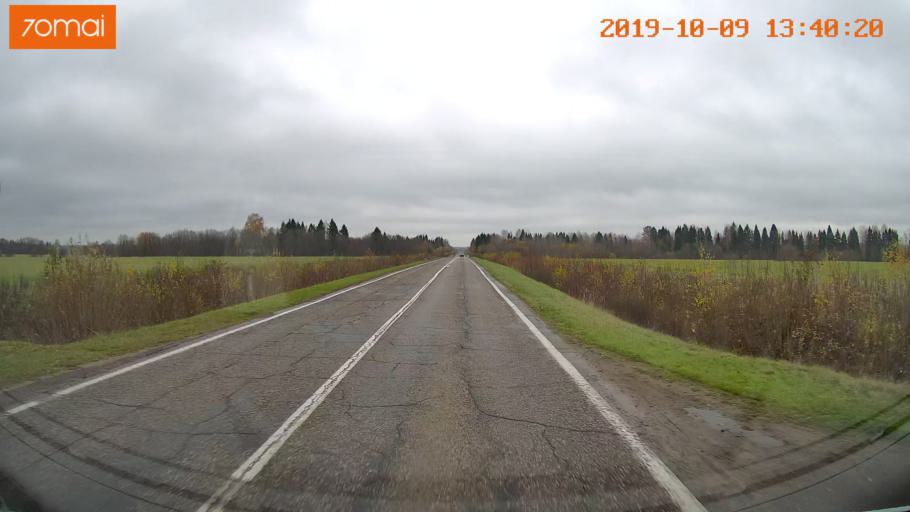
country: RU
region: Kostroma
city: Buy
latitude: 58.3471
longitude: 41.1446
